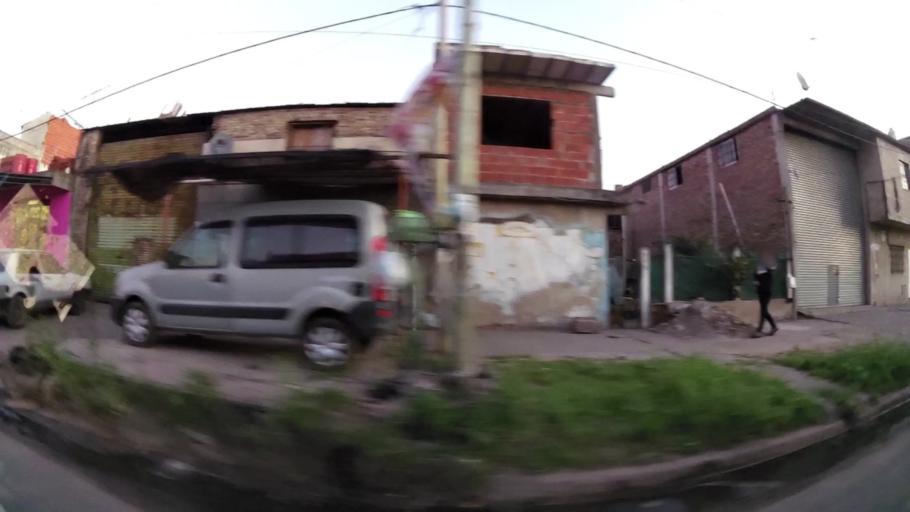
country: AR
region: Buenos Aires
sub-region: Partido de Moron
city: Moron
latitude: -34.7028
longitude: -58.6132
